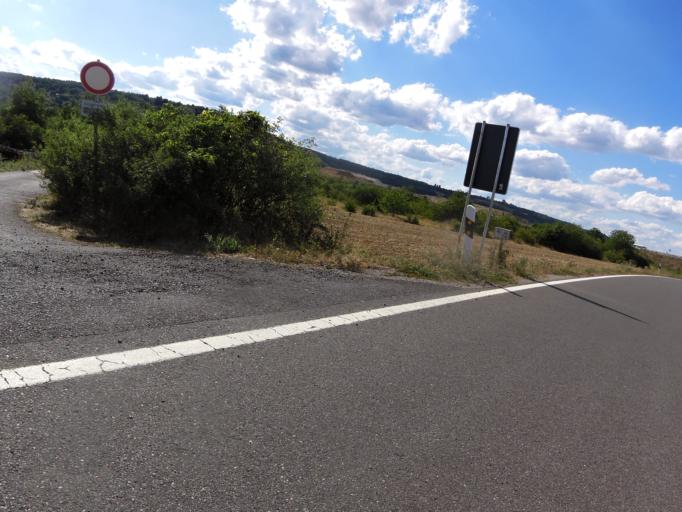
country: DE
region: Bavaria
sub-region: Regierungsbezirk Unterfranken
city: Eibelstadt
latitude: 49.7378
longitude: 9.9999
